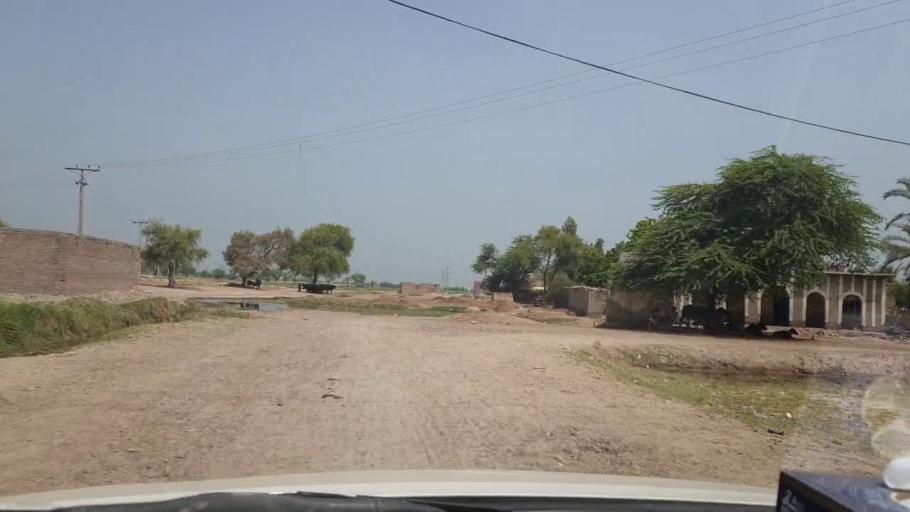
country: PK
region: Sindh
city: Shikarpur
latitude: 27.9928
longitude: 68.6959
